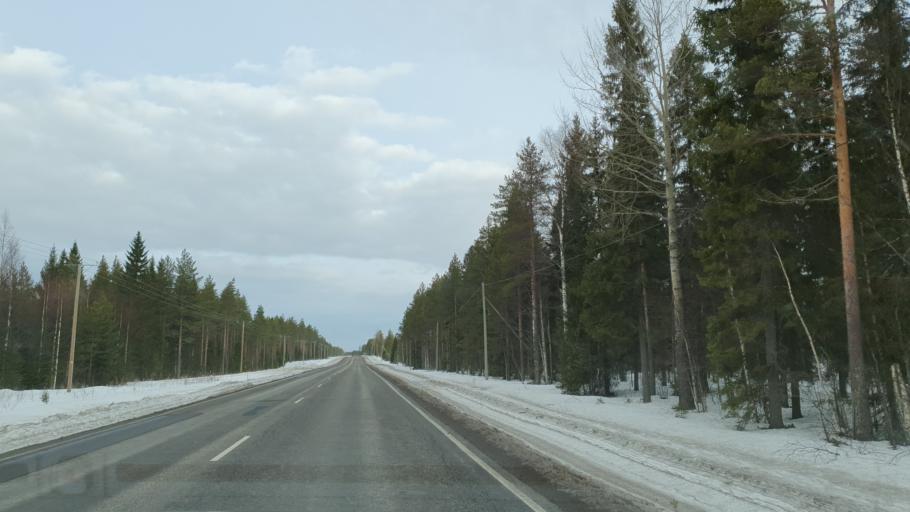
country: FI
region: Kainuu
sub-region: Kajaani
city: Vuokatti
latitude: 64.2090
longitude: 28.1435
